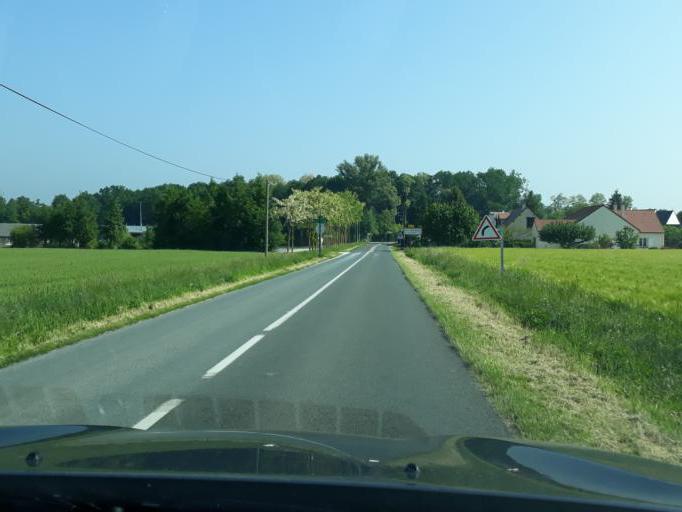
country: FR
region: Centre
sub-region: Departement du Loiret
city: Boigny-sur-Bionne
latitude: 47.9253
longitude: 2.0249
